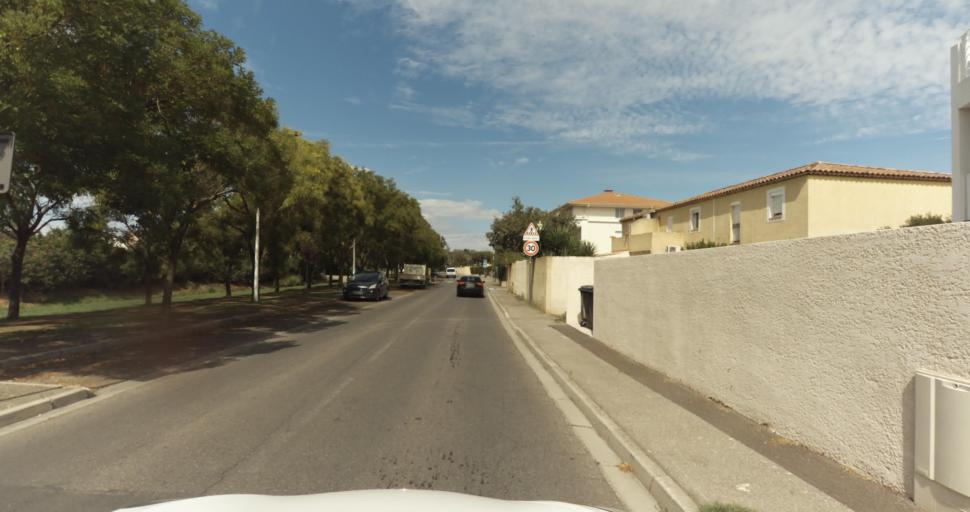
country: FR
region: Provence-Alpes-Cote d'Azur
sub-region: Departement des Bouches-du-Rhone
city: Miramas
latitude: 43.5886
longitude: 5.0140
